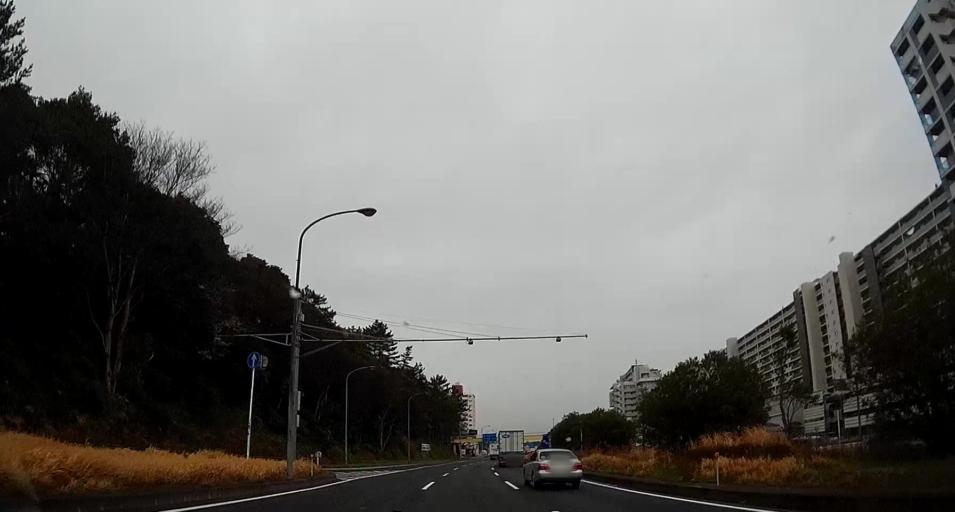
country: JP
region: Chiba
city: Chiba
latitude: 35.6404
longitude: 140.0748
